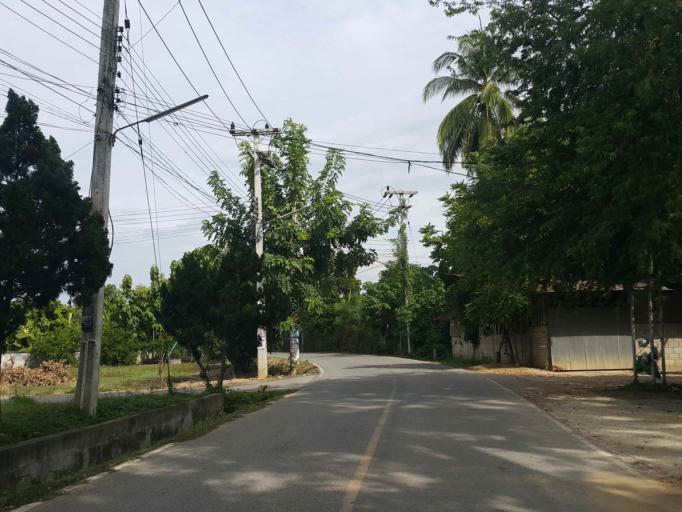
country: TH
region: Chiang Mai
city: Saraphi
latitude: 18.7417
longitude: 99.0566
